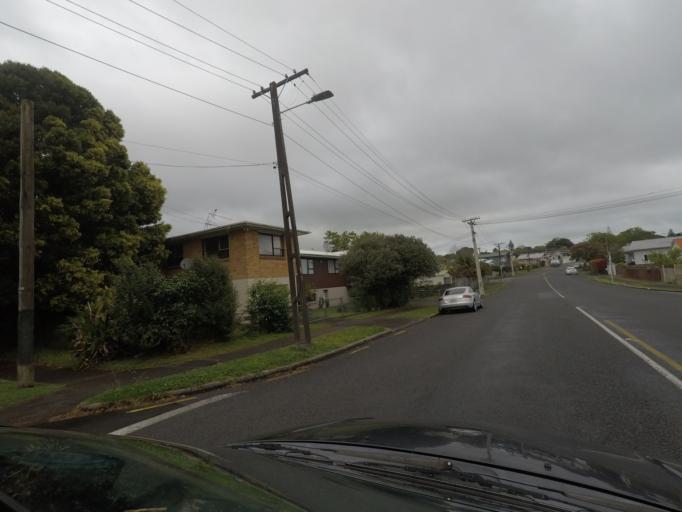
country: NZ
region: Auckland
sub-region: Auckland
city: Auckland
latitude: -36.8895
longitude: 174.7321
